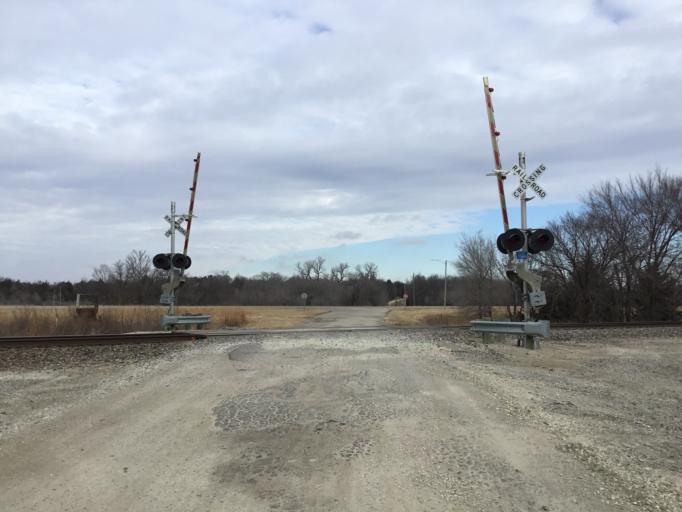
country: US
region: Kansas
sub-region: Chase County
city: Cottonwood Falls
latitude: 38.3004
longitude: -96.7413
